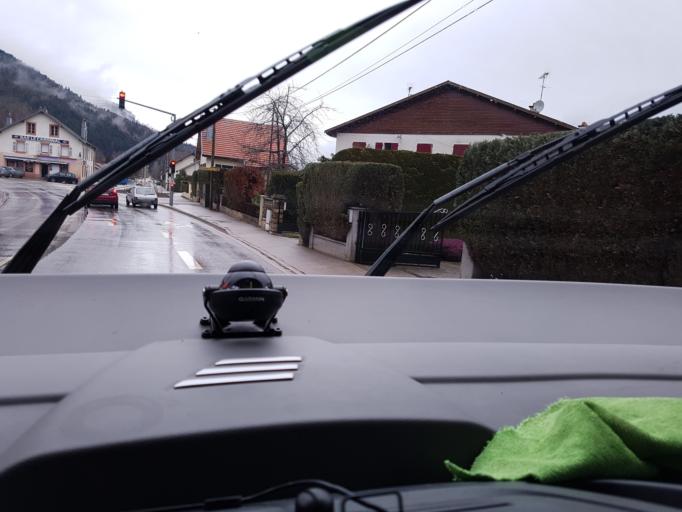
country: FR
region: Lorraine
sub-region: Departement des Vosges
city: Saint-Die-des-Vosges
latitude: 48.2886
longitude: 6.9271
